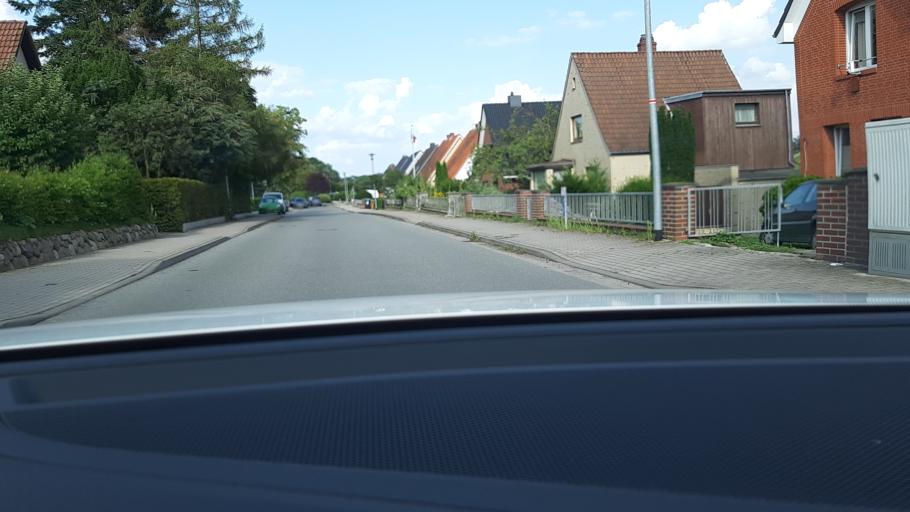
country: DE
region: Schleswig-Holstein
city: Reinfeld
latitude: 53.8359
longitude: 10.5029
